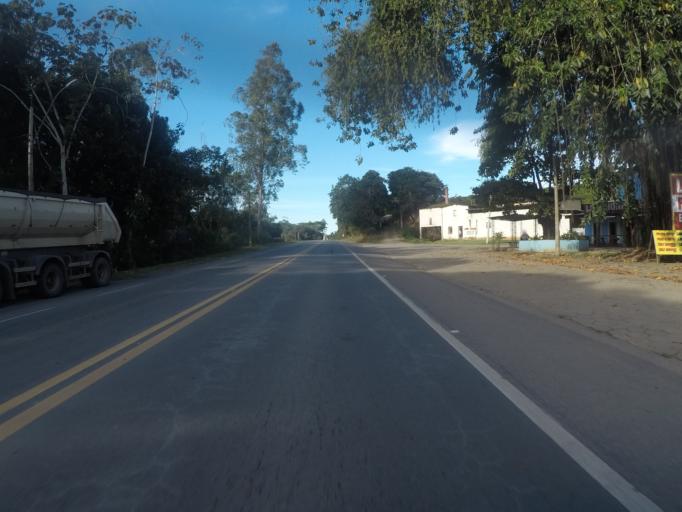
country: BR
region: Espirito Santo
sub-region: Ibiracu
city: Ibiracu
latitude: -19.8681
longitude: -40.4052
